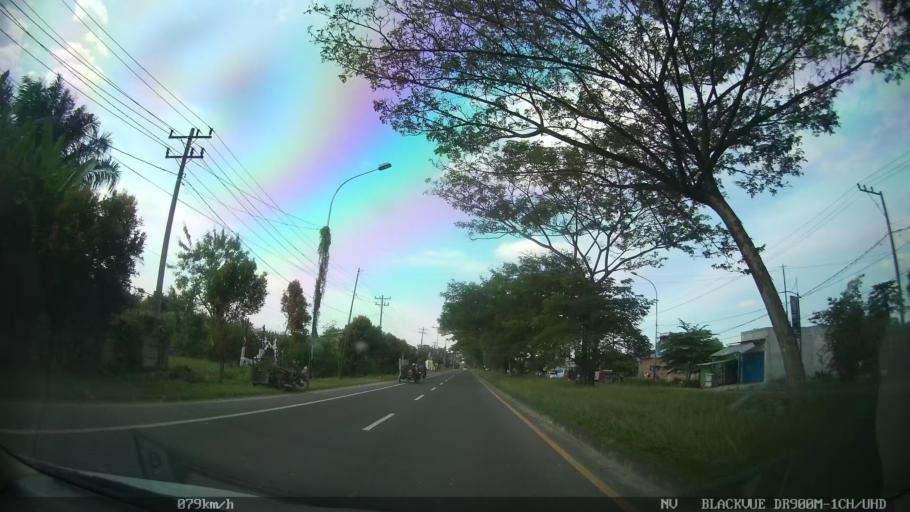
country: ID
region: North Sumatra
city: Percut
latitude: 3.5690
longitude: 98.7965
